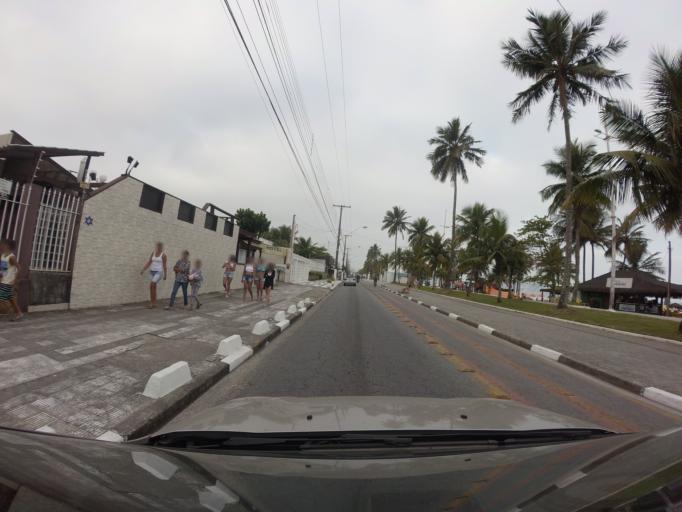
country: BR
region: Sao Paulo
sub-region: Guaruja
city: Guaruja
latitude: -23.9880
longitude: -46.2351
